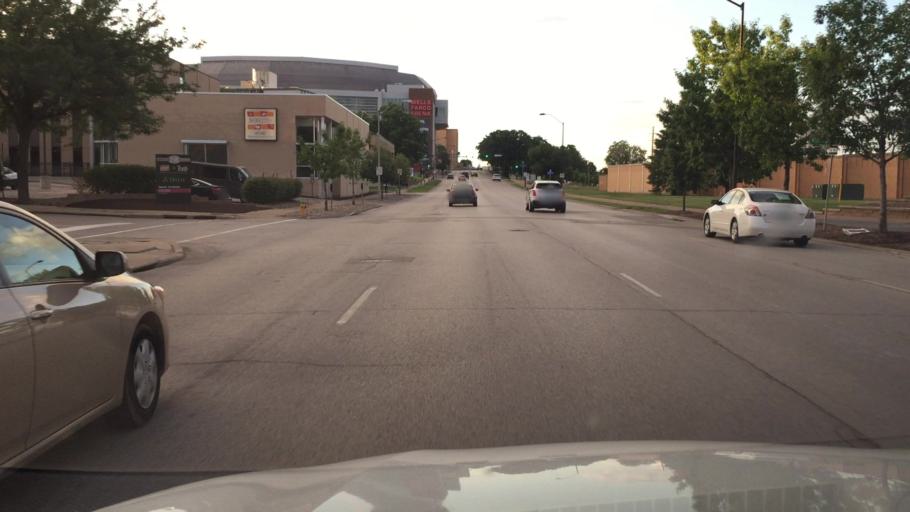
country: US
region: Iowa
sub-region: Polk County
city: Des Moines
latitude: 41.5895
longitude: -93.6204
